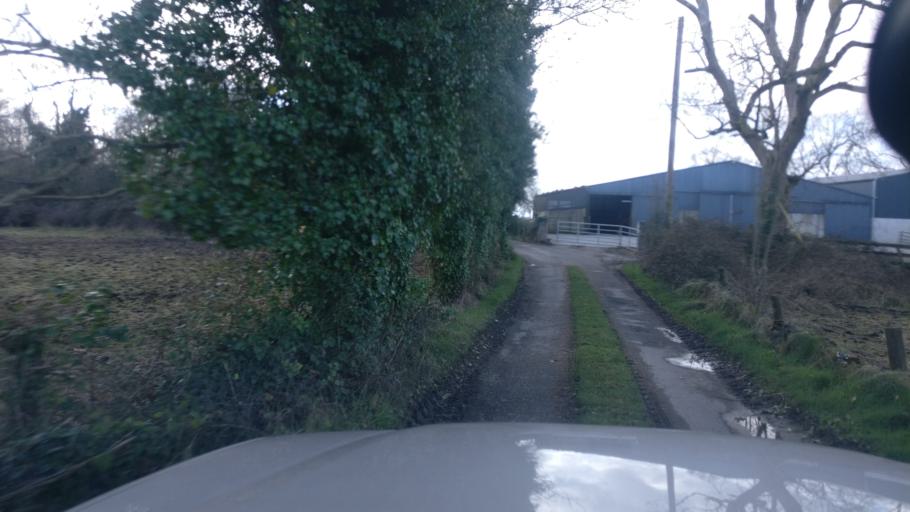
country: IE
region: Connaught
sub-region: County Galway
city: Loughrea
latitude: 53.1832
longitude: -8.4334
